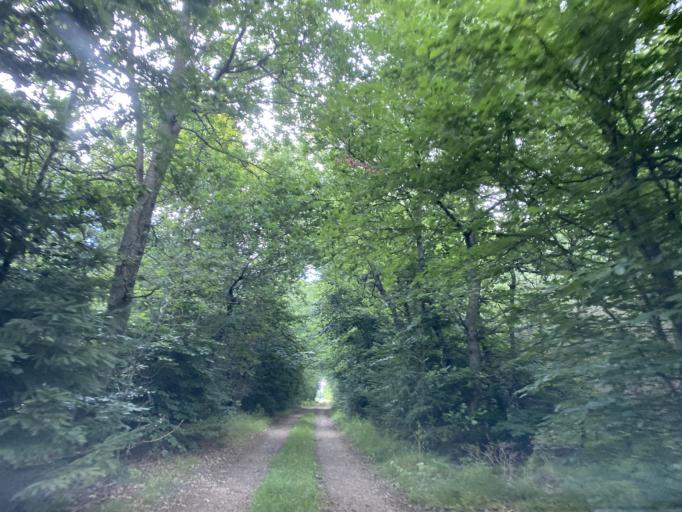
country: DK
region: Central Jutland
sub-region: Viborg Kommune
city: Bjerringbro
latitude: 56.2788
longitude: 9.6562
